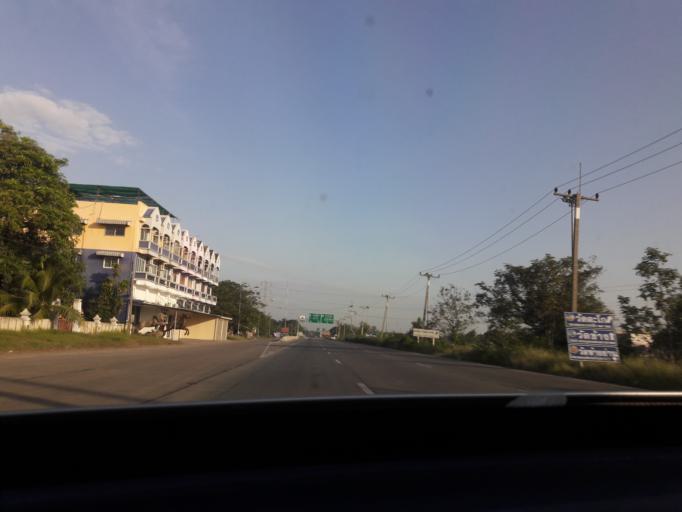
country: TH
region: Phra Nakhon Si Ayutthaya
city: Bang Pahan
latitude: 14.4528
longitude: 100.5395
